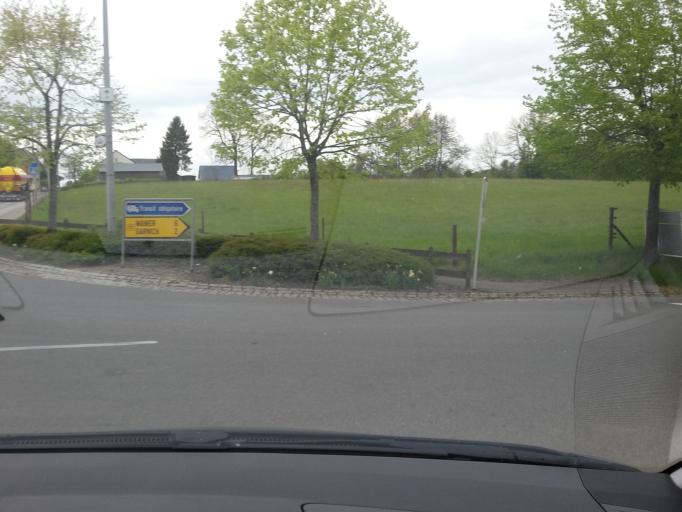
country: LU
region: Luxembourg
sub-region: Canton de Capellen
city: Garnich
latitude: 49.6035
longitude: 5.9271
